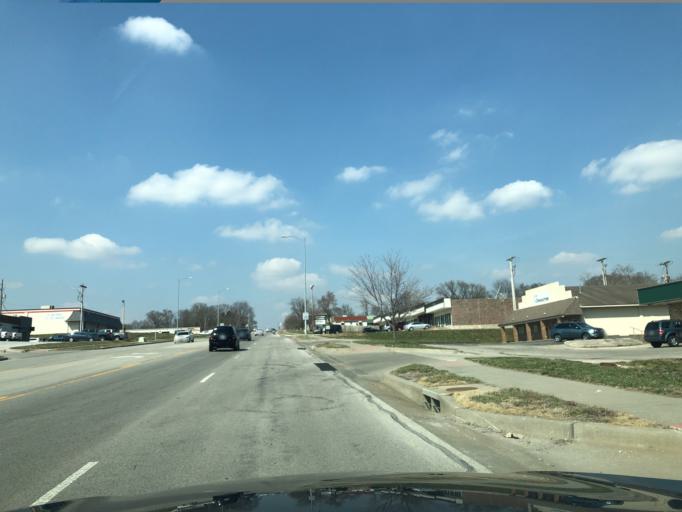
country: US
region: Missouri
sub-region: Platte County
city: Riverside
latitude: 39.1784
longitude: -94.6133
